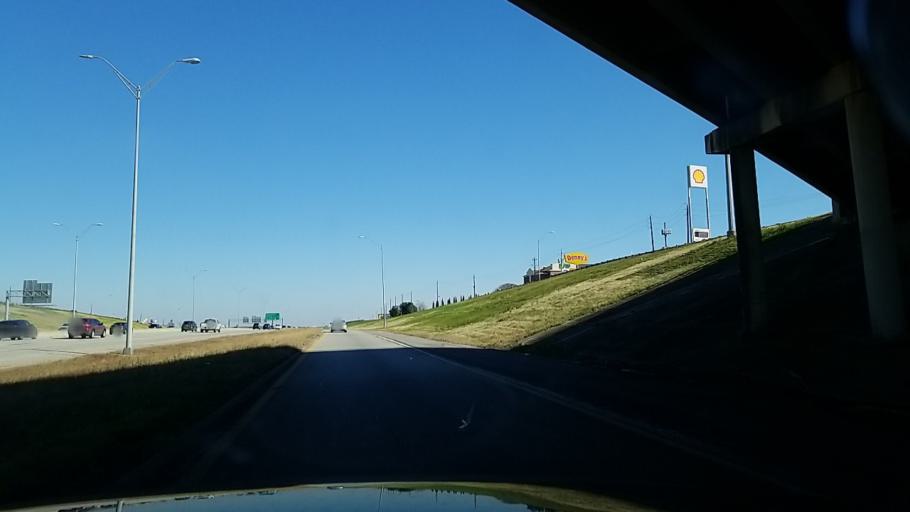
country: US
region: Texas
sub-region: Tarrant County
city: Sansom Park
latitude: 32.8137
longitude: -97.4125
